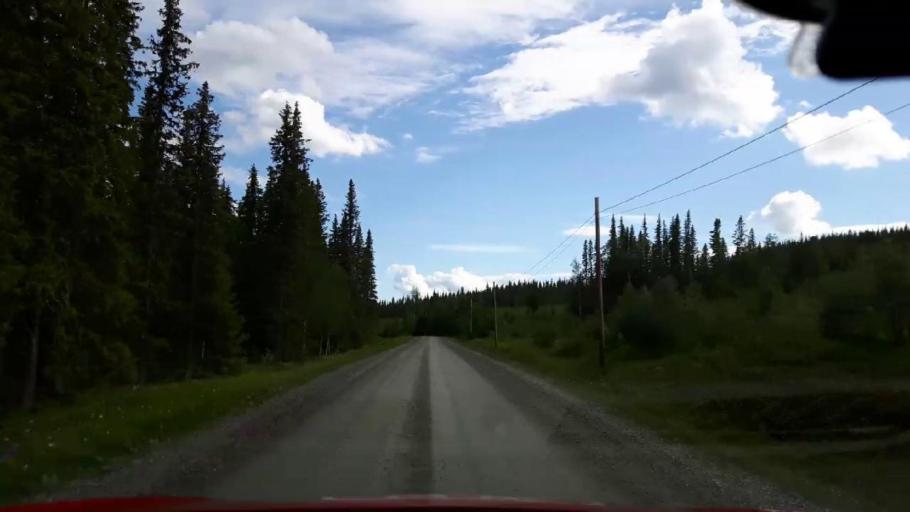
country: SE
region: Jaemtland
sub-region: Krokoms Kommun
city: Valla
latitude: 63.8225
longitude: 14.0409
